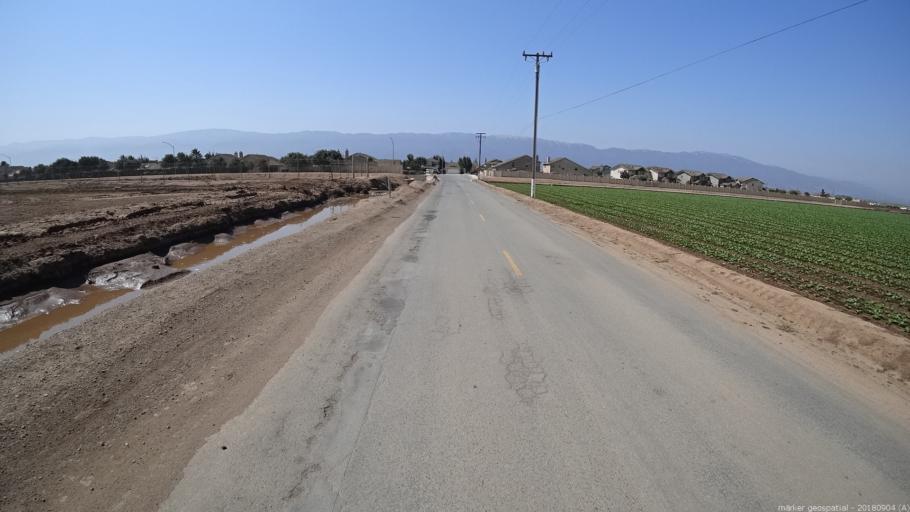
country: US
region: California
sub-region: Monterey County
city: Gonzales
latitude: 36.5264
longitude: -121.4450
